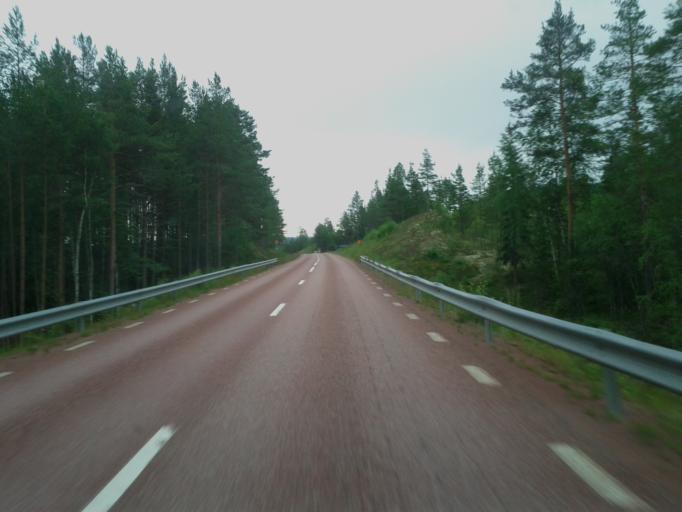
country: SE
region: Dalarna
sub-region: Alvdalens Kommun
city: AElvdalen
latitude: 61.2838
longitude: 13.7549
